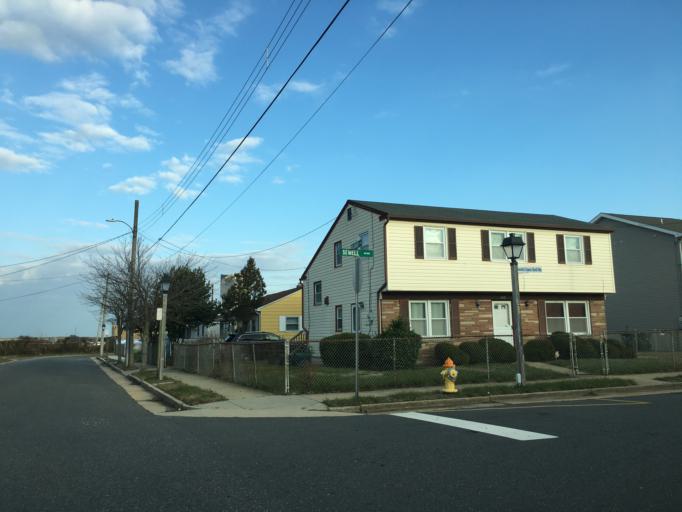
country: US
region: New Jersey
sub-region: Atlantic County
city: Atlantic City
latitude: 39.3725
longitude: -74.4255
